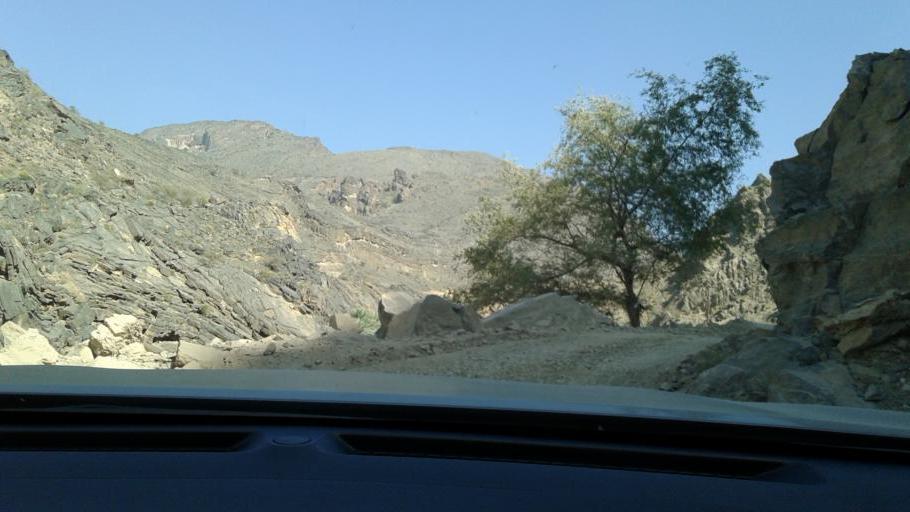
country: OM
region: Al Batinah
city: Bayt al `Awabi
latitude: 23.1943
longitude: 57.3917
